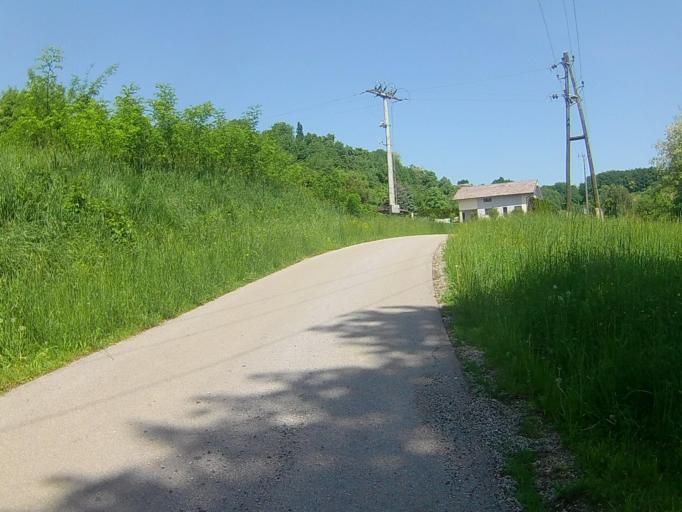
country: SI
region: Pesnica
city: Pesnica pri Mariboru
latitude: 46.5667
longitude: 15.7046
